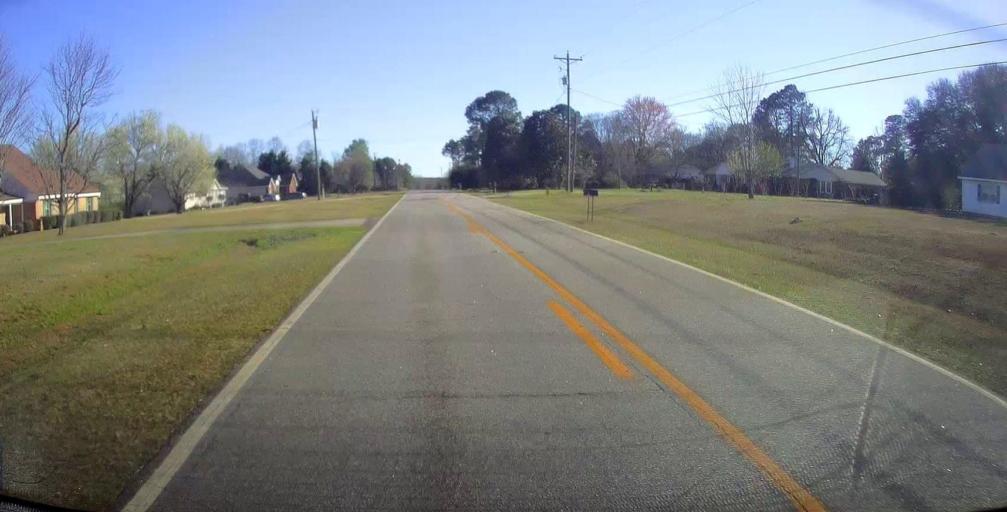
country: US
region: Georgia
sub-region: Peach County
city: Fort Valley
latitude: 32.5646
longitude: -83.9159
